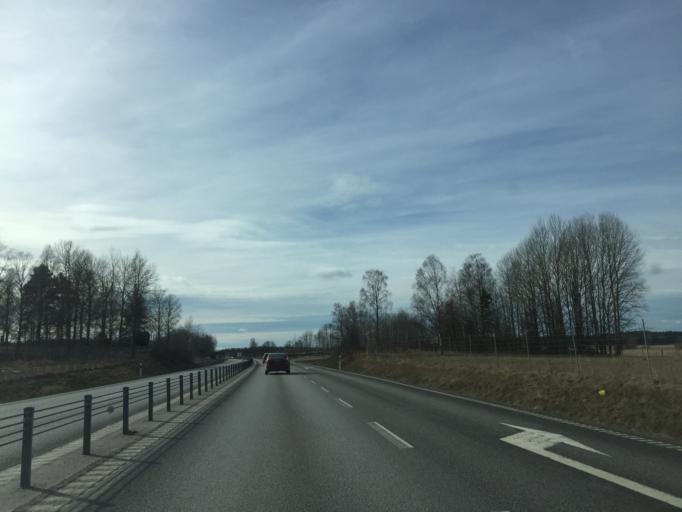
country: SE
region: Vaestmanland
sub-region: Kopings Kommun
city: Koping
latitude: 59.5719
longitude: 16.0978
